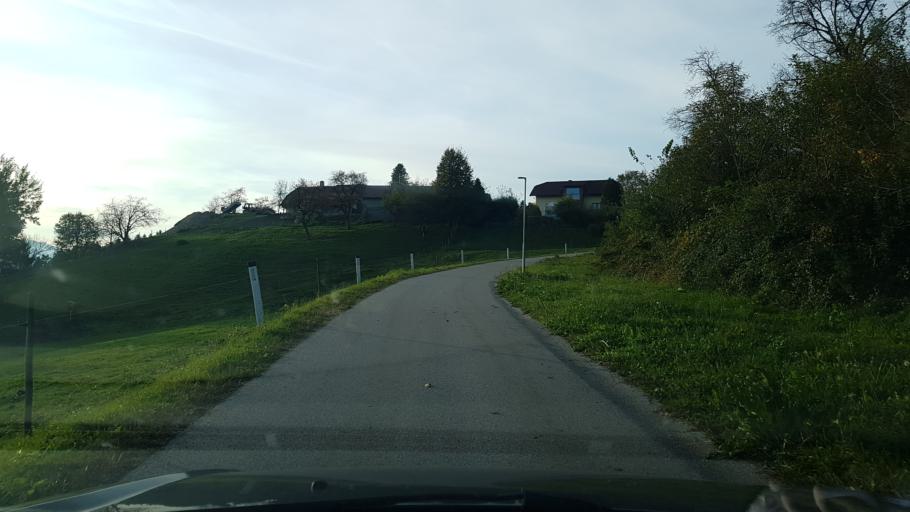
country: SI
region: Slovenj Gradec
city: Smartno pri Slovenj Gradcu
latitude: 46.5067
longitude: 15.1068
